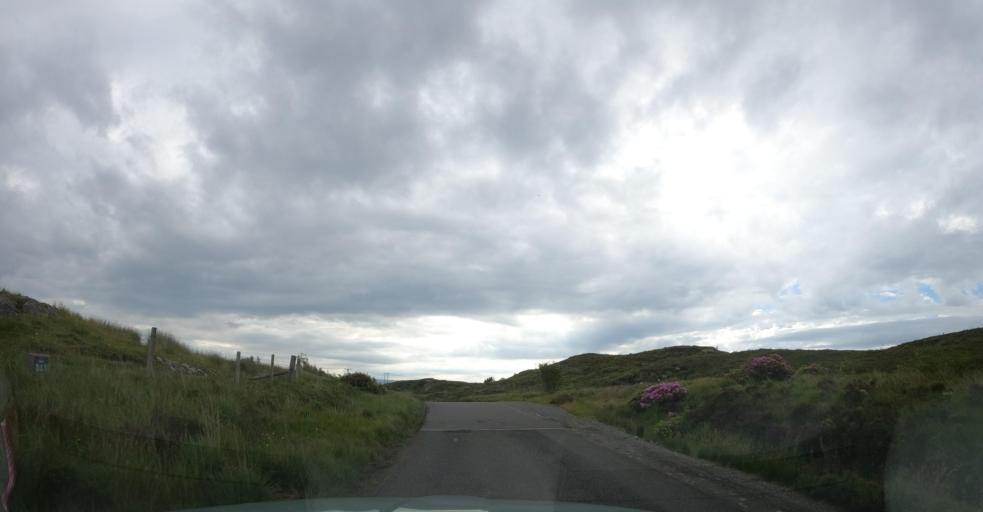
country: GB
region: Scotland
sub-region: Eilean Siar
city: Stornoway
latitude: 58.2007
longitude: -6.4052
